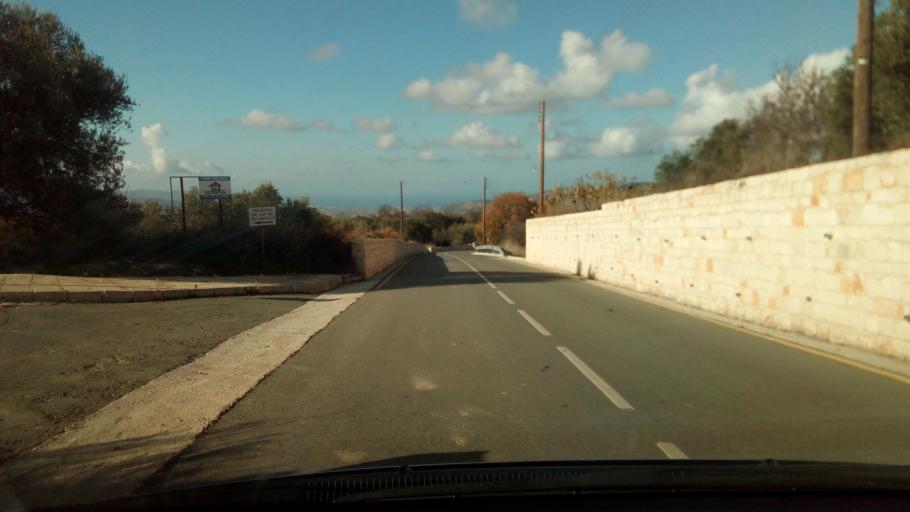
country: CY
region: Pafos
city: Tala
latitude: 34.9262
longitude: 32.5242
